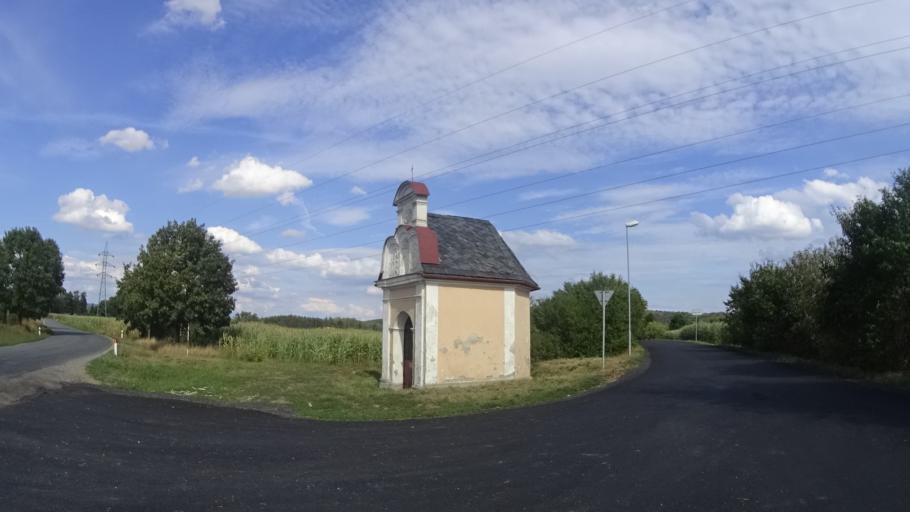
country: CZ
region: Olomoucky
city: Moravicany
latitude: 49.7789
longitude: 16.9468
